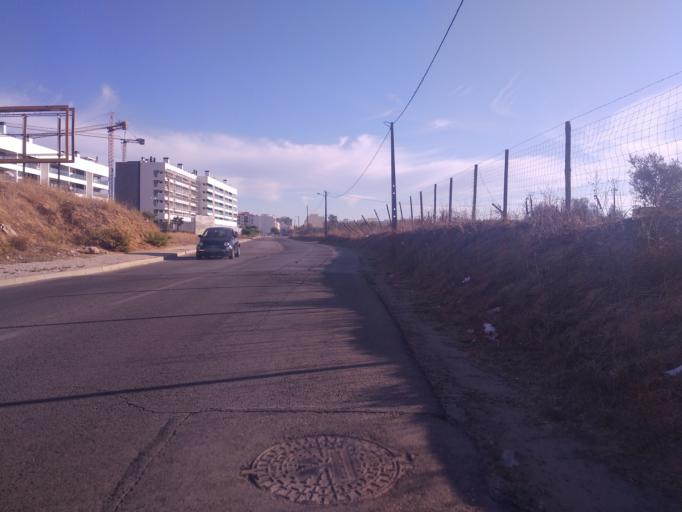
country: PT
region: Faro
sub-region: Faro
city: Faro
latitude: 37.0322
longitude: -7.9400
